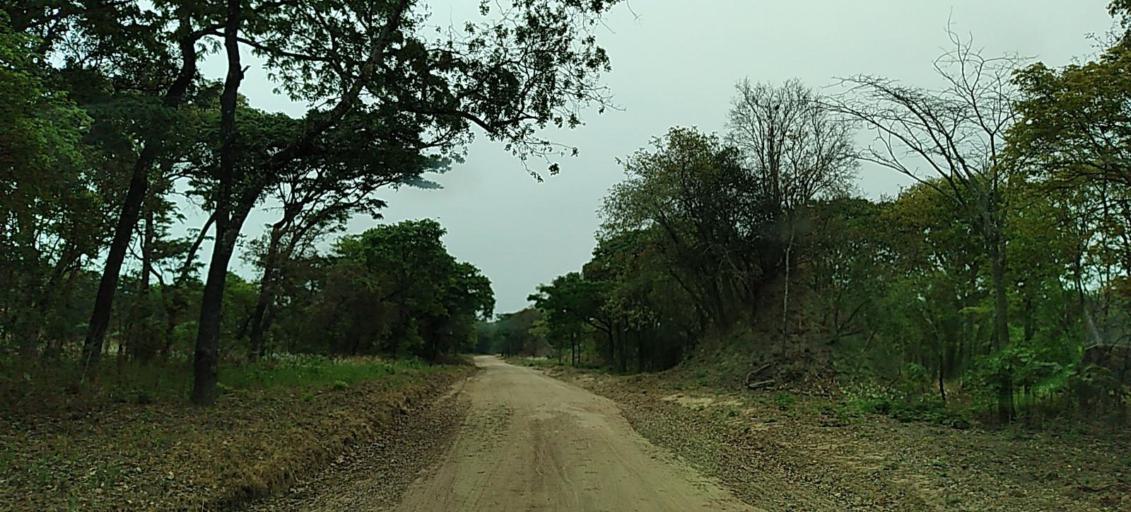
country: ZM
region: North-Western
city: Solwezi
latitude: -12.5293
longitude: 26.5229
